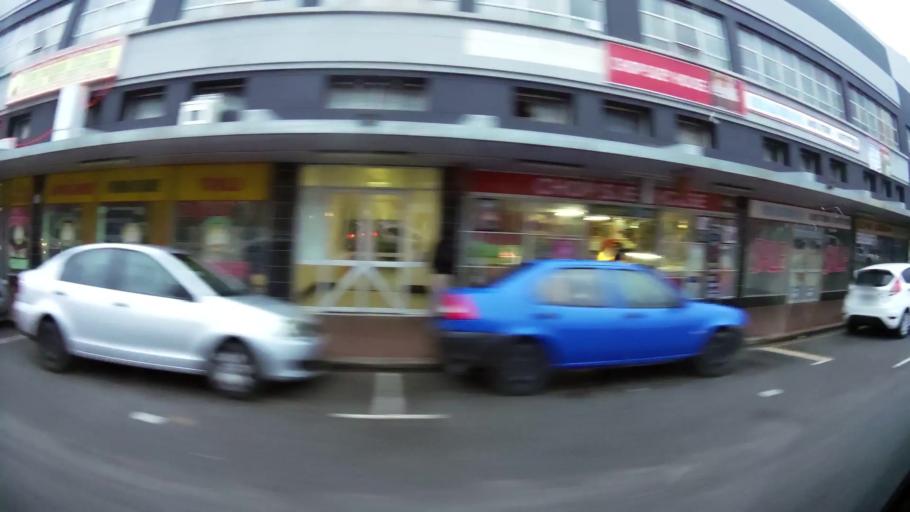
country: ZA
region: Eastern Cape
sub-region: Nelson Mandela Bay Metropolitan Municipality
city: Port Elizabeth
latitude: -33.9462
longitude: 25.6064
